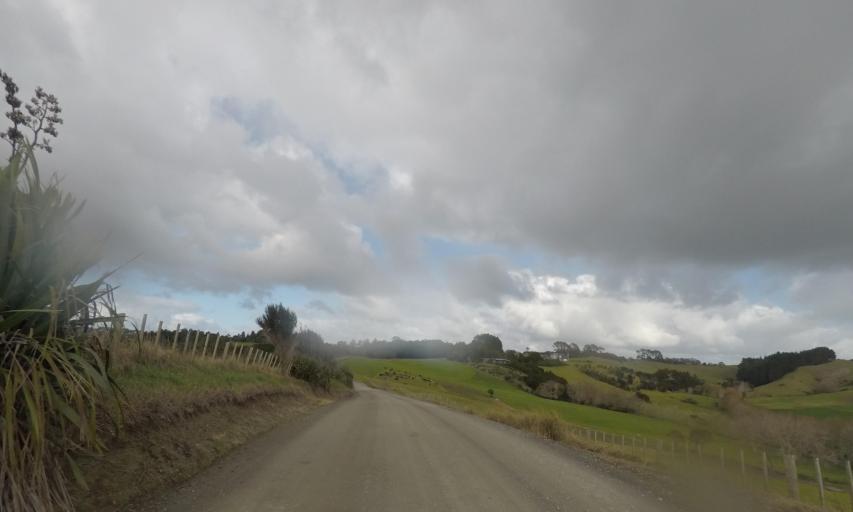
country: NZ
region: Auckland
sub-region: Auckland
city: Wellsford
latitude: -36.1654
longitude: 174.6024
